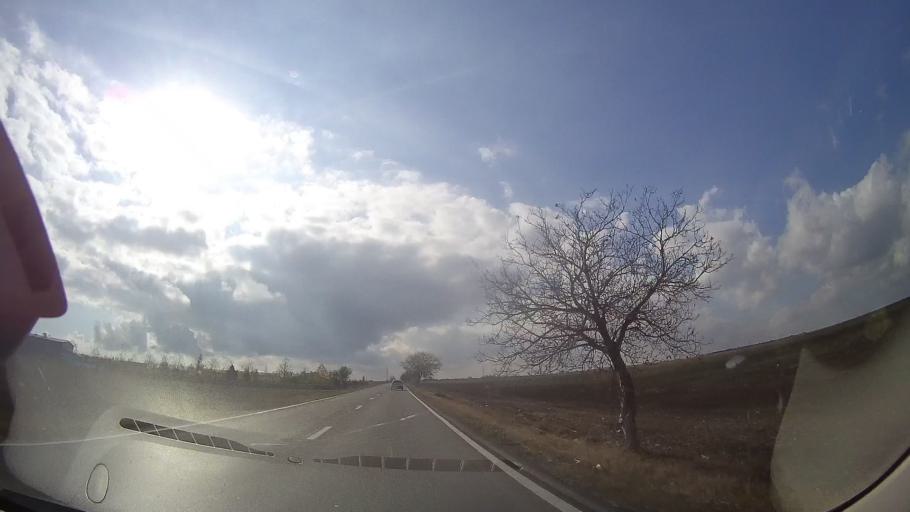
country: RO
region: Constanta
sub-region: Comuna Agigea
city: Agigea
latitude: 44.0801
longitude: 28.6034
